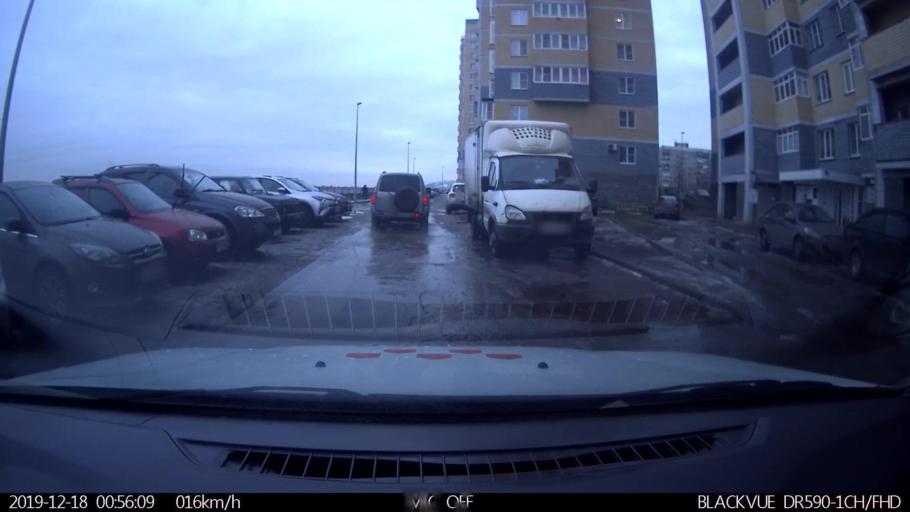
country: RU
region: Nizjnij Novgorod
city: Nizhniy Novgorod
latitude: 56.3495
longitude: 43.9299
